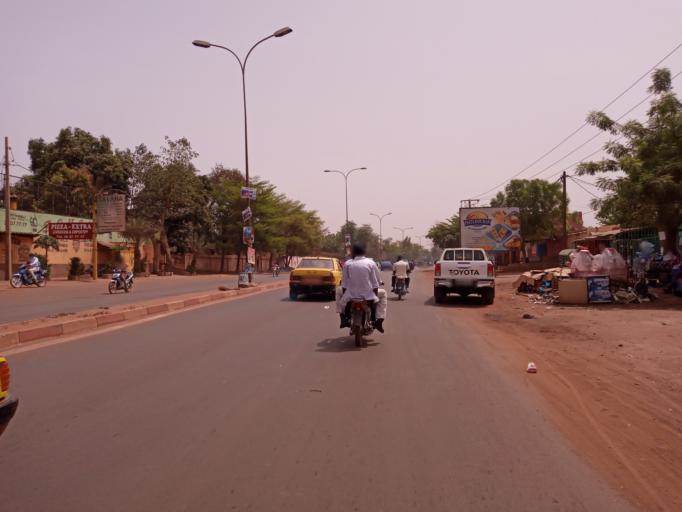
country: ML
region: Bamako
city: Bamako
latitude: 12.6627
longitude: -7.9514
